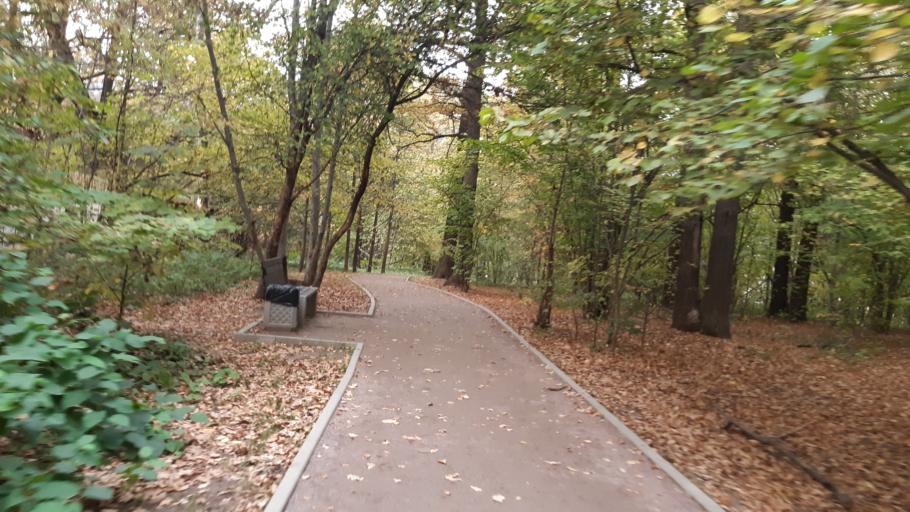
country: RU
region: Moscow
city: Vagonoremont
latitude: 55.9031
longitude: 37.5639
